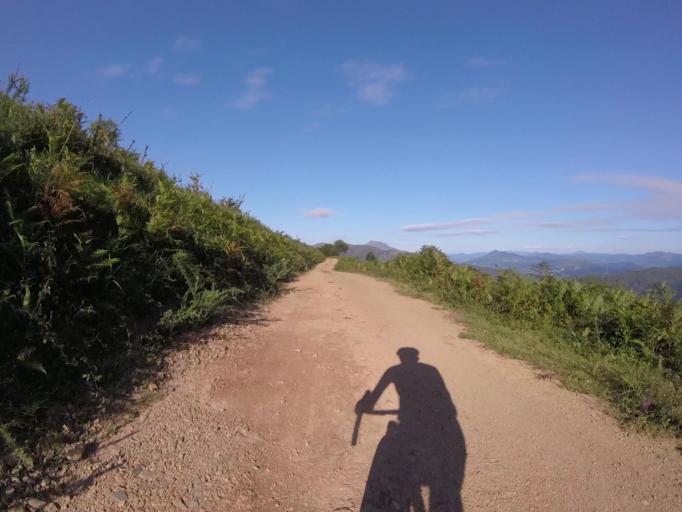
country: ES
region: Basque Country
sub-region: Provincia de Guipuzcoa
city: Irun
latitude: 43.2997
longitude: -1.7482
